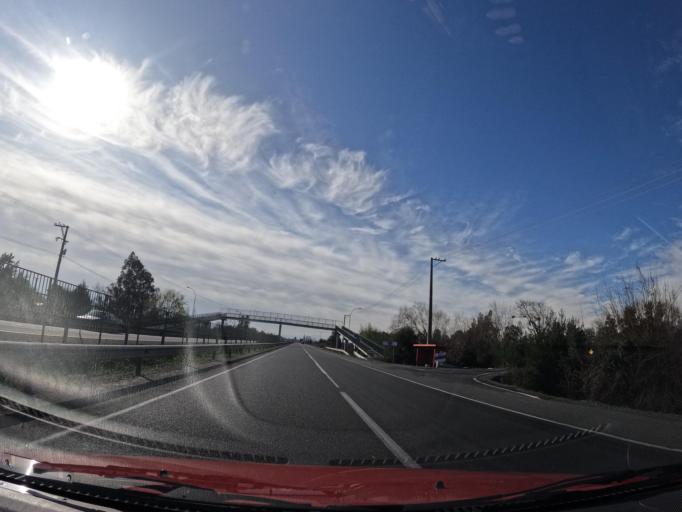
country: CL
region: Biobio
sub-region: Provincia de Nuble
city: San Carlos
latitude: -36.3475
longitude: -71.8542
